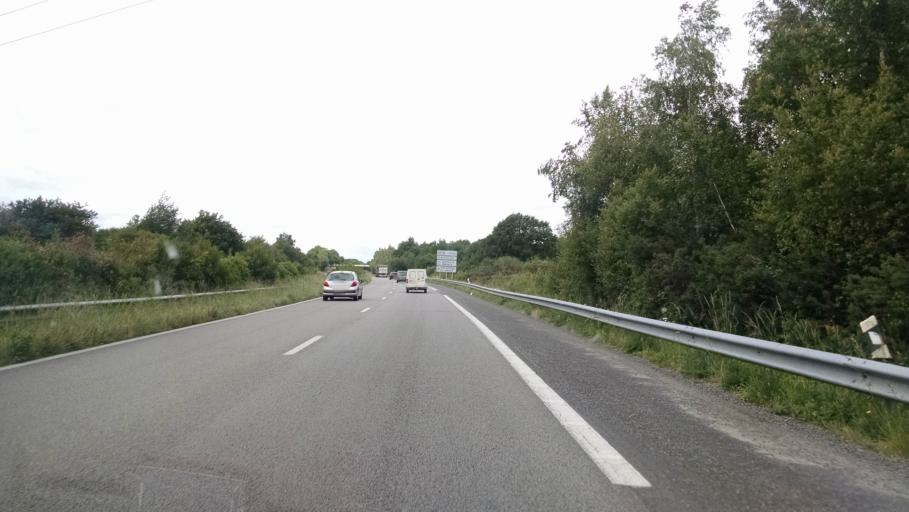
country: FR
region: Pays de la Loire
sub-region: Departement de la Loire-Atlantique
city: Missillac
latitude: 47.4704
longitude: -2.1647
